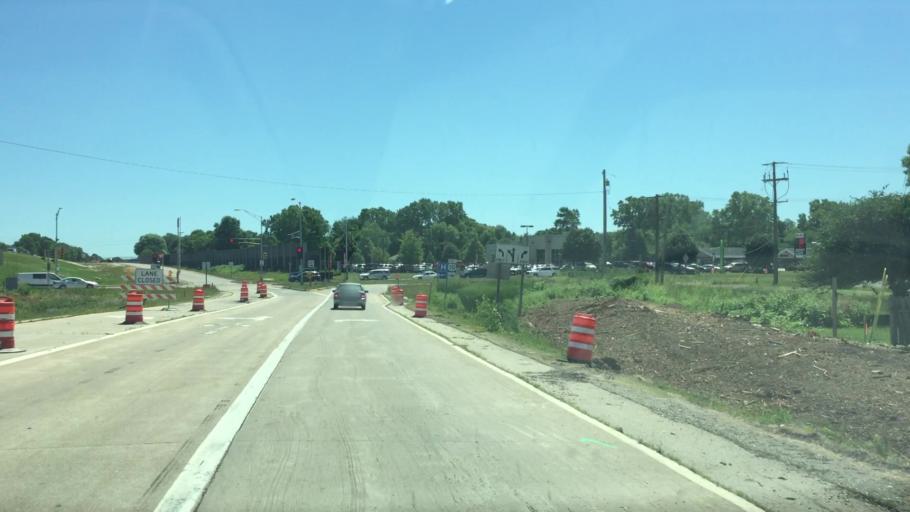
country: US
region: Wisconsin
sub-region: Outagamie County
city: Appleton
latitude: 44.2332
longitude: -88.4055
